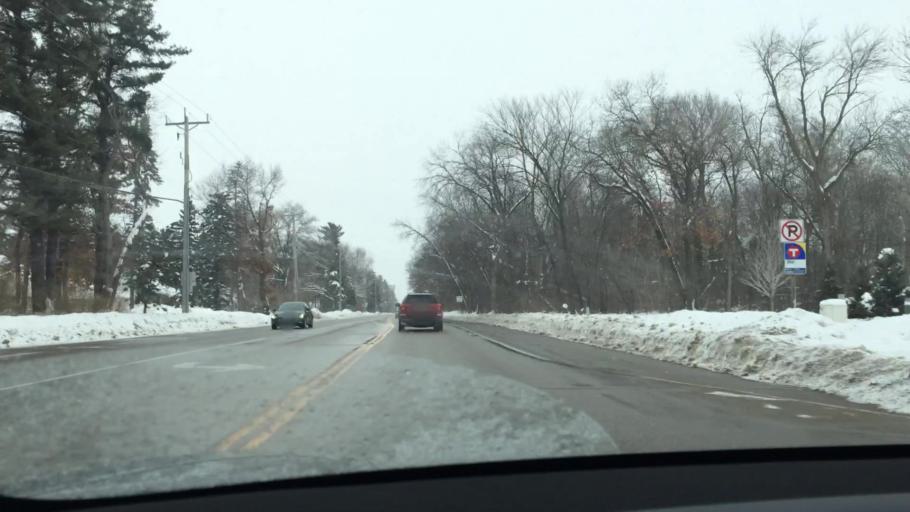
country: US
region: Minnesota
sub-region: Ramsey County
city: Shoreview
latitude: 45.0951
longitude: -93.1271
